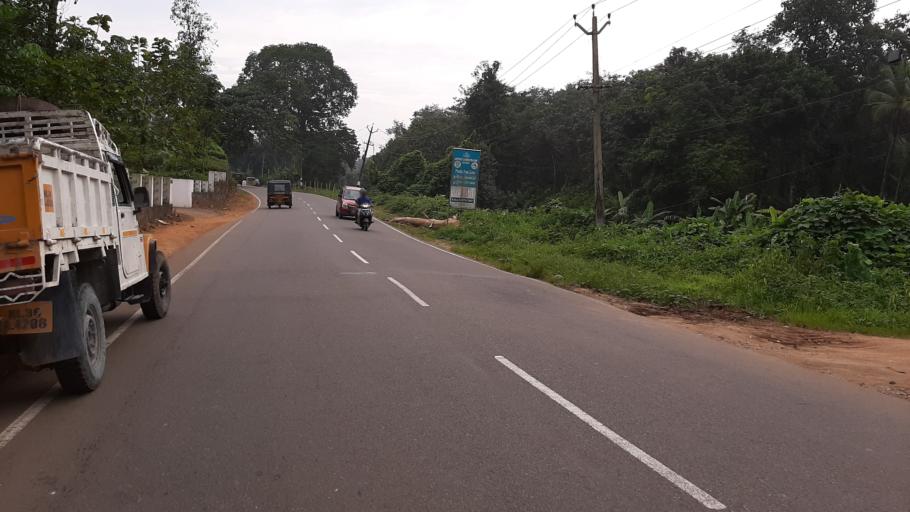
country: IN
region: Kerala
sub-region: Kottayam
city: Erattupetta
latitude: 9.4932
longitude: 76.8494
